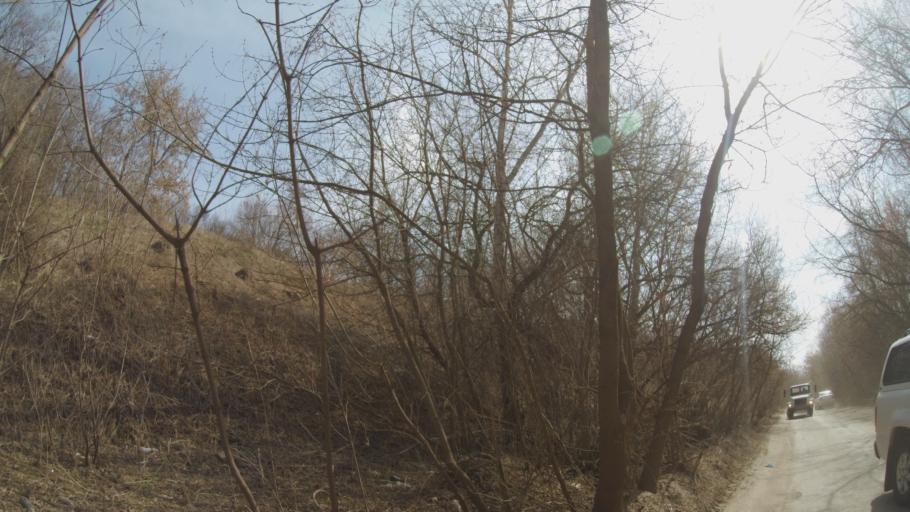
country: RU
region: Nizjnij Novgorod
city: Vyyezdnoye
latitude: 55.3890
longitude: 43.8095
